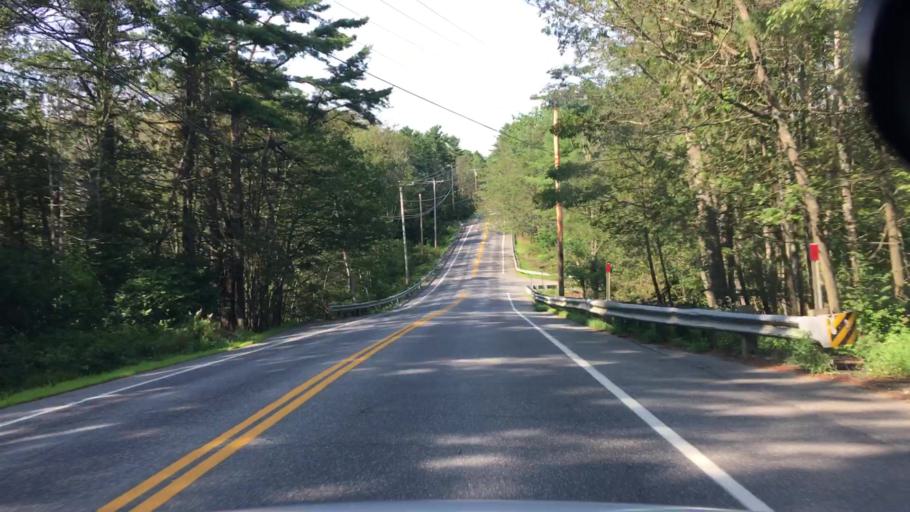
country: US
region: Maine
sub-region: Cumberland County
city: Harpswell Center
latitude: 43.8207
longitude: -69.9210
